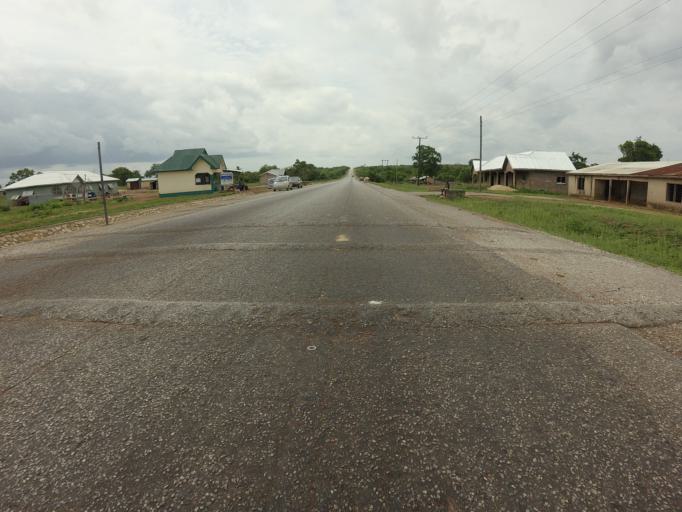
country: GH
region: Brong-Ahafo
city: Kintampo
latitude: 8.6648
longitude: -1.5191
